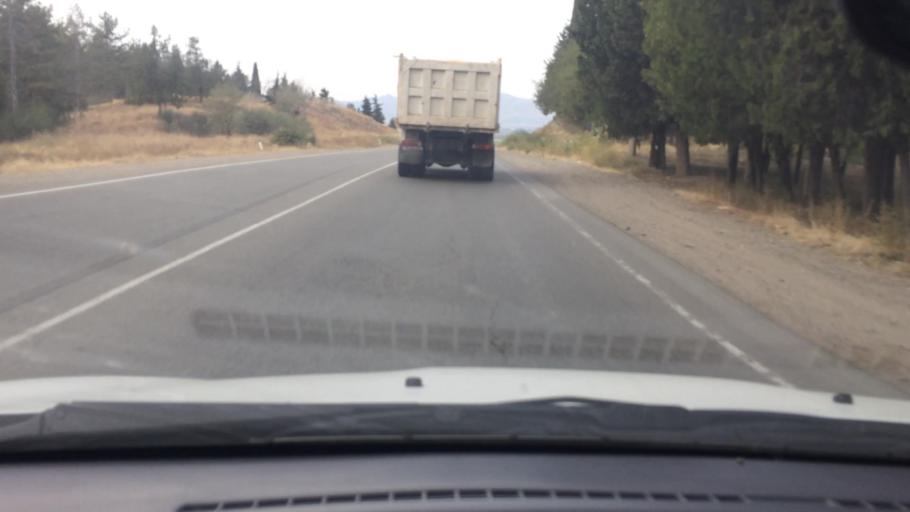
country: GE
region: Kvemo Kartli
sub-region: Marneuli
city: Marneuli
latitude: 41.5224
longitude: 44.7788
